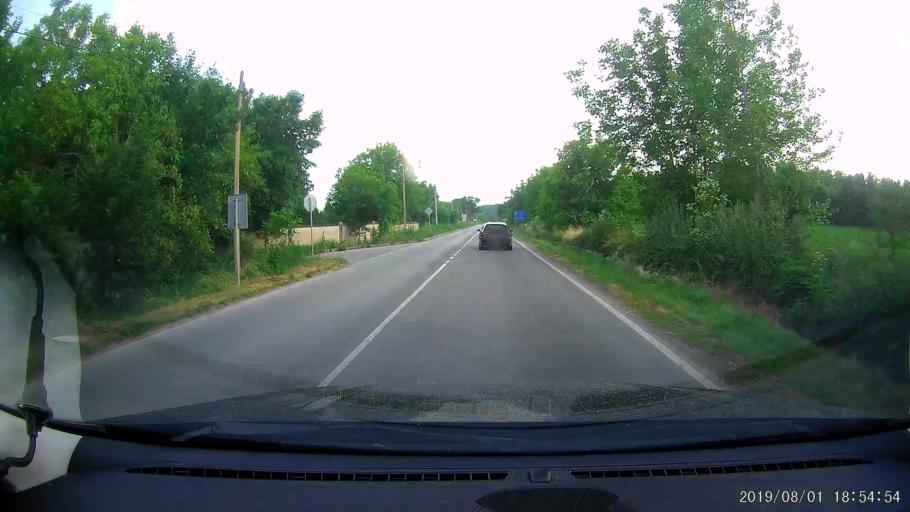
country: BG
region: Shumen
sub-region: Obshtina Shumen
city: Shumen
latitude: 43.1892
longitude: 27.0034
